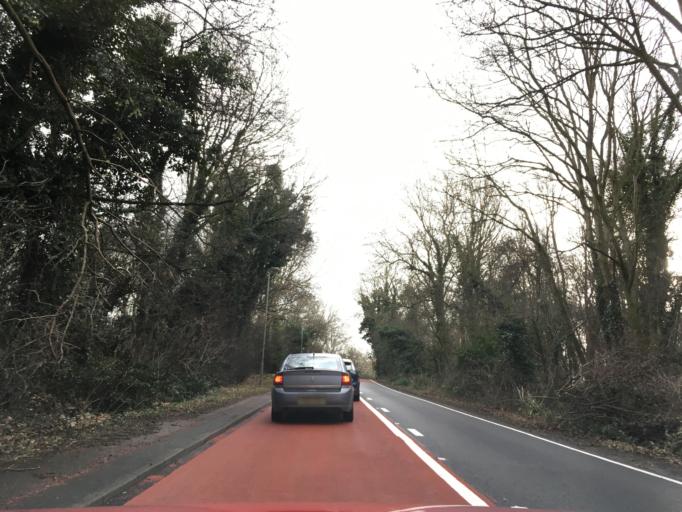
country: GB
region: England
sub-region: Nottinghamshire
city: Gotham
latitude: 52.8540
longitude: -1.1925
